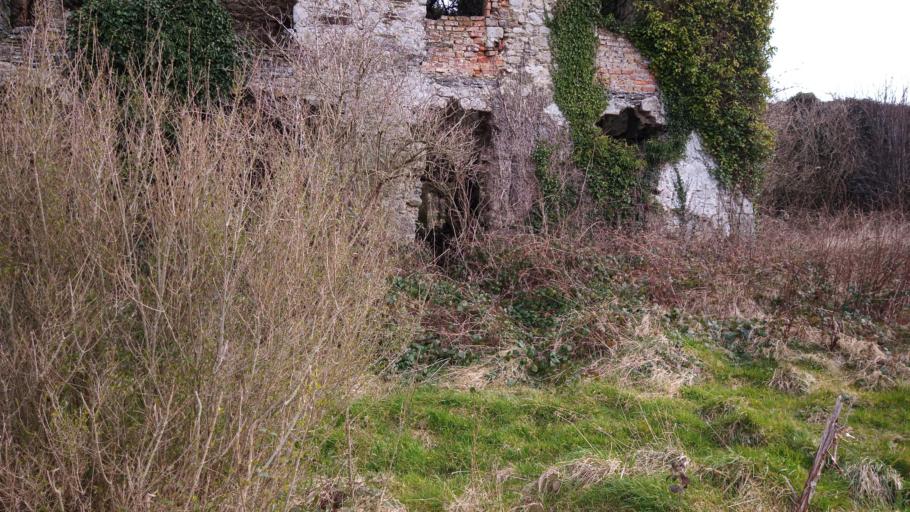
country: IE
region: Leinster
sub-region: Loch Garman
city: Enniscorthy
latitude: 52.4776
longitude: -6.7196
